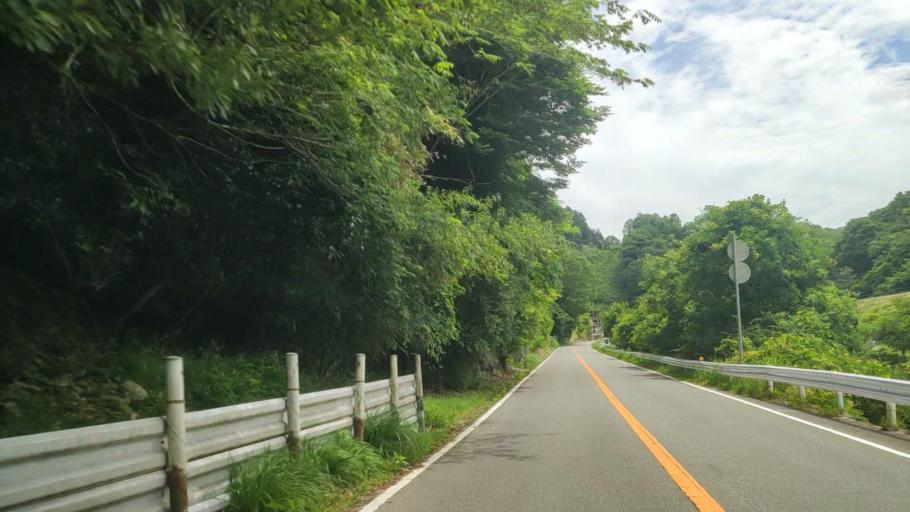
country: JP
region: Hyogo
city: Yamazakicho-nakabirose
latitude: 35.0771
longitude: 134.3591
